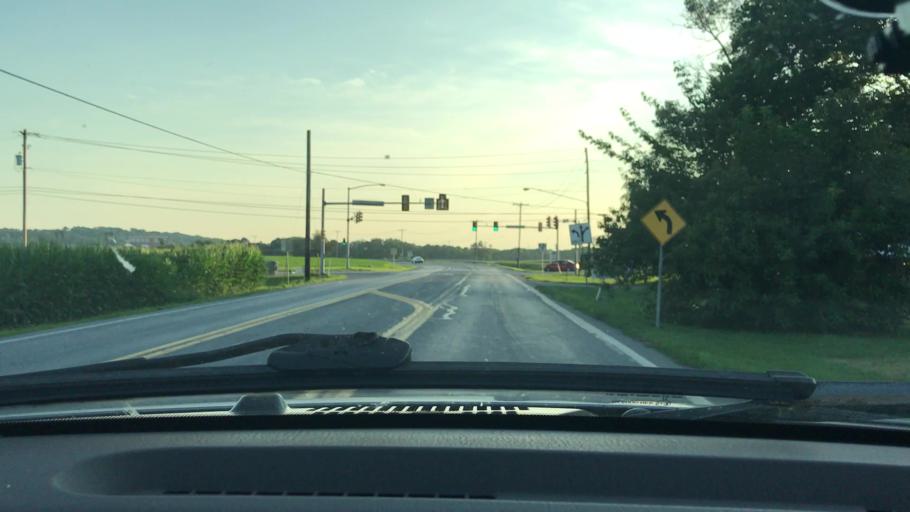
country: US
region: Pennsylvania
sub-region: Lancaster County
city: East Petersburg
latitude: 40.0944
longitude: -76.3766
